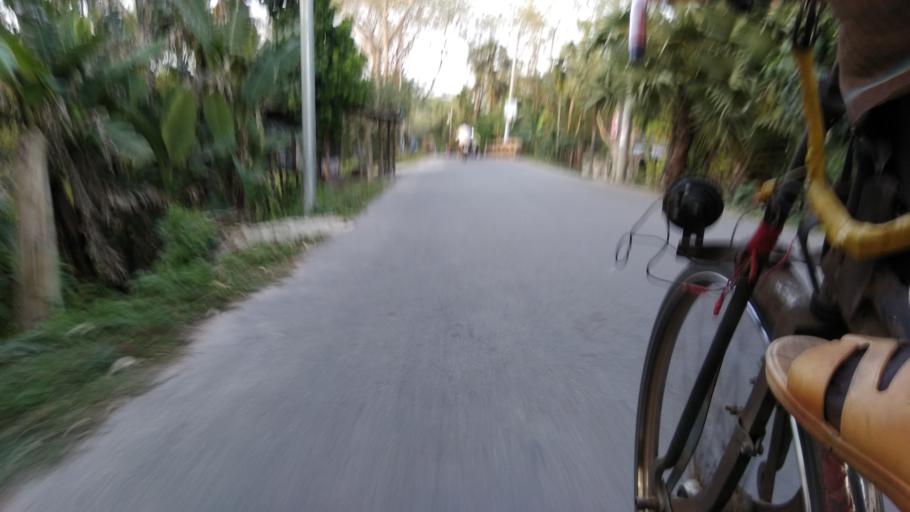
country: BD
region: Barisal
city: Mehendiganj
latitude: 22.9325
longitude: 90.4054
